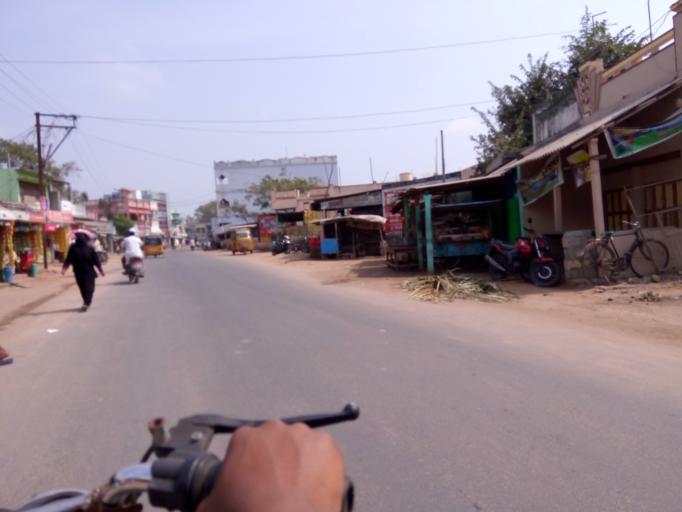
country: IN
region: Andhra Pradesh
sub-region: Prakasam
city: Chirala
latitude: 15.8495
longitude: 80.3874
